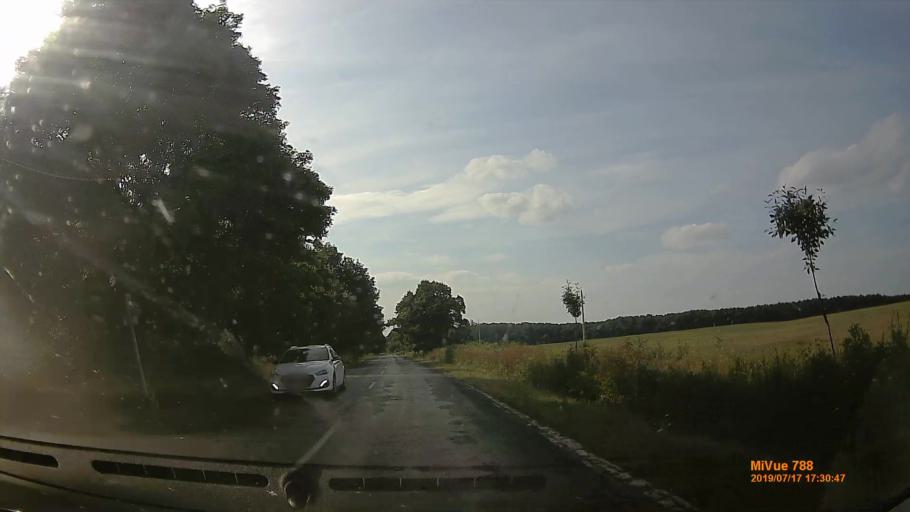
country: HU
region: Veszprem
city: Ajka
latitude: 47.0272
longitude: 17.5699
